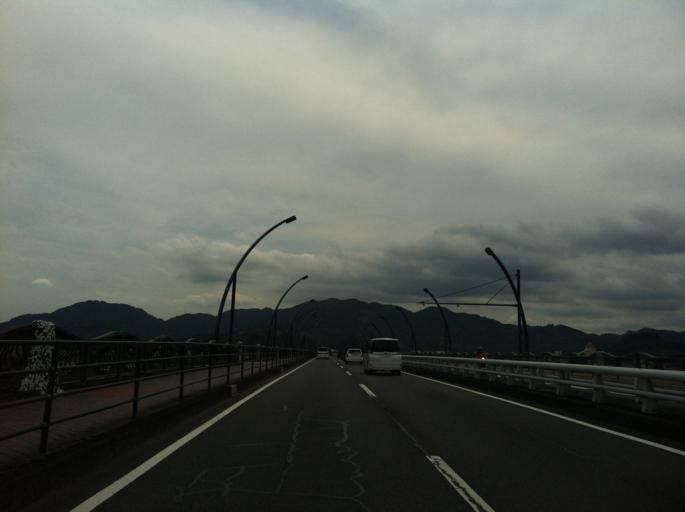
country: JP
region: Shizuoka
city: Shizuoka-shi
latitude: 34.9542
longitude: 138.3817
